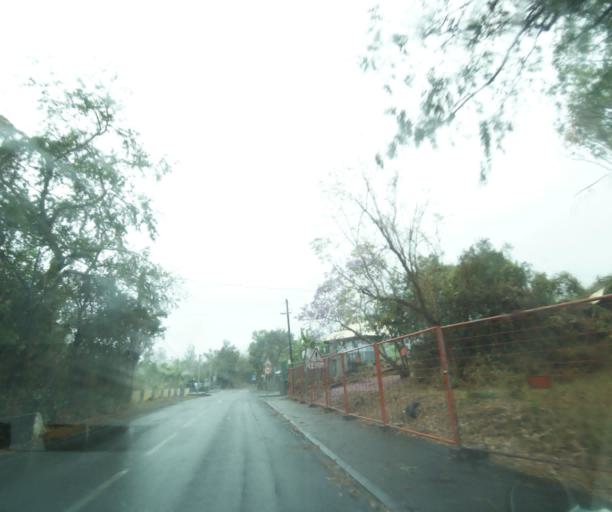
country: RE
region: Reunion
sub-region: Reunion
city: Saint-Paul
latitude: -21.0176
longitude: 55.3033
